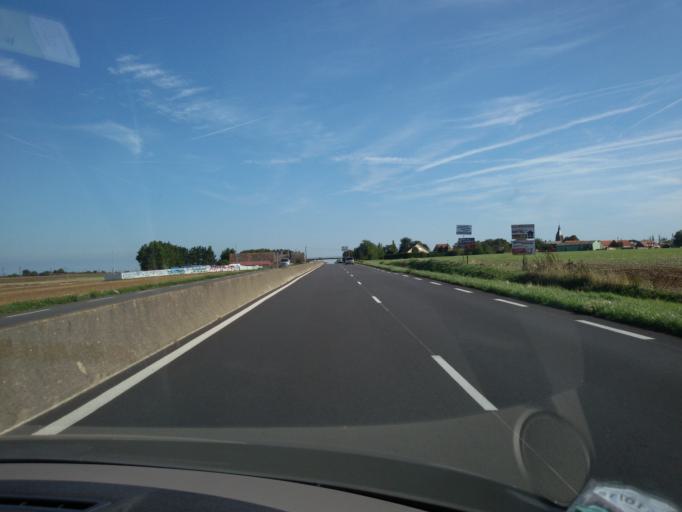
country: FR
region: Ile-de-France
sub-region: Departement de l'Essonne
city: Pussay
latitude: 48.3421
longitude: 2.0378
